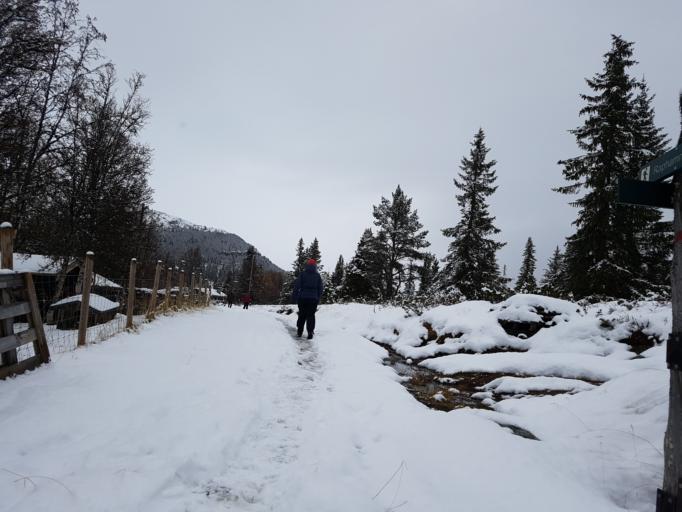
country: NO
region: Oppland
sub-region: Sel
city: Otta
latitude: 61.8077
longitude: 9.6811
